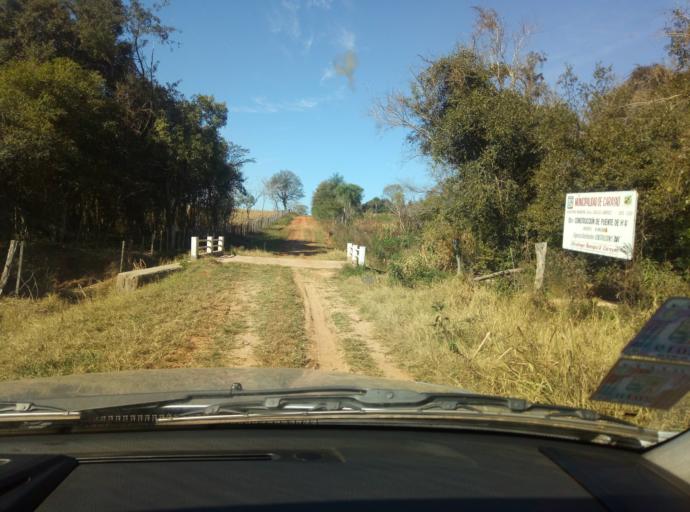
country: PY
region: Caaguazu
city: Carayao
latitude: -25.1690
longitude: -56.3072
